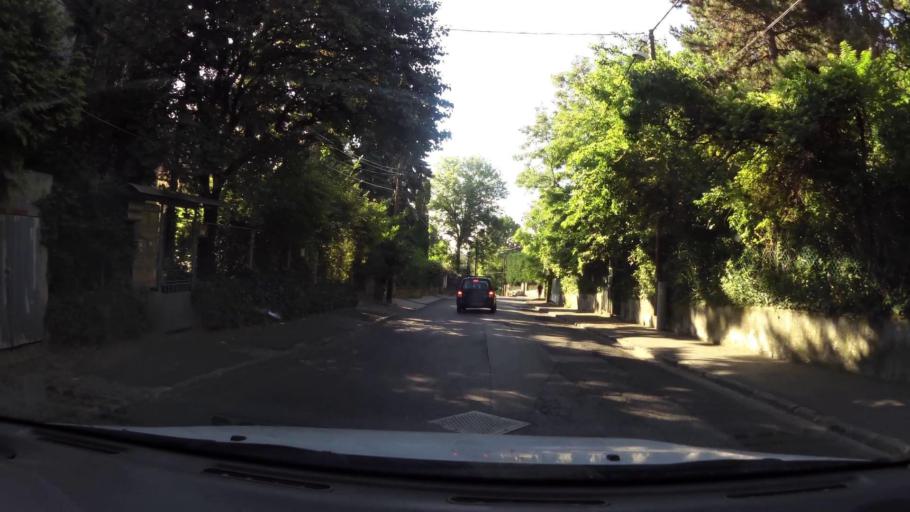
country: HU
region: Budapest
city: Budapest XII. keruelet
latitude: 47.5224
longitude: 18.9841
